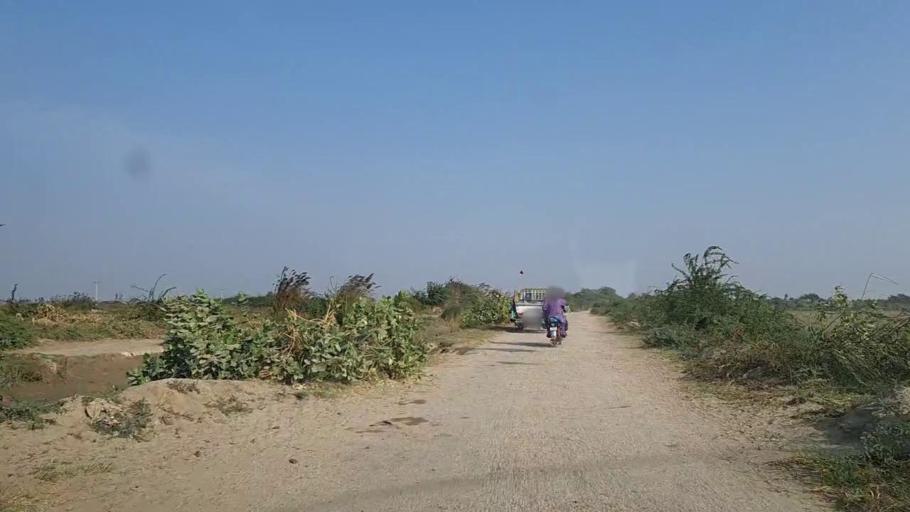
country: PK
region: Sindh
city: Mirpur Sakro
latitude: 24.5947
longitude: 67.6117
